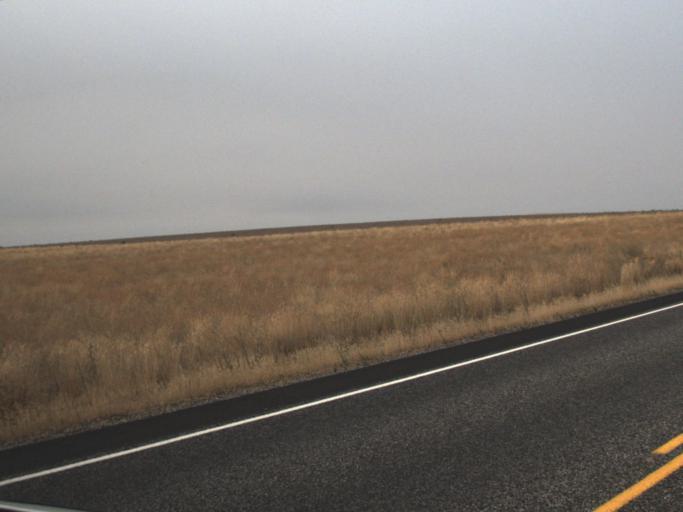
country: US
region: Washington
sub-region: Benton County
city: Benton City
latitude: 46.1784
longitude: -119.6009
